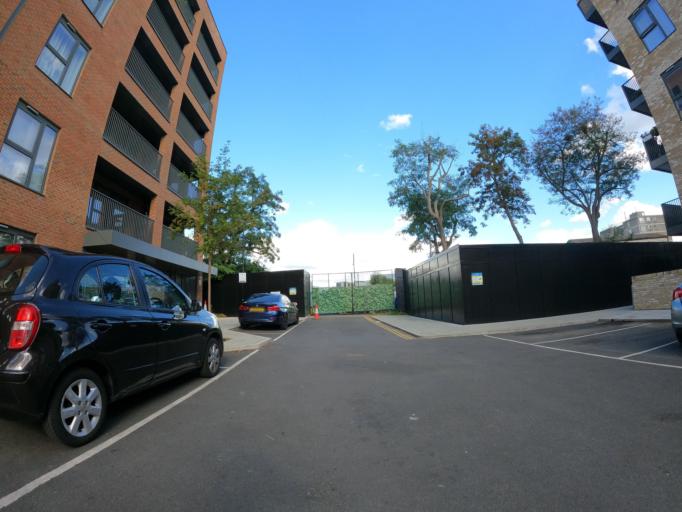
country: GB
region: England
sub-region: Greater London
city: Ealing
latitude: 51.5119
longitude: -0.3259
